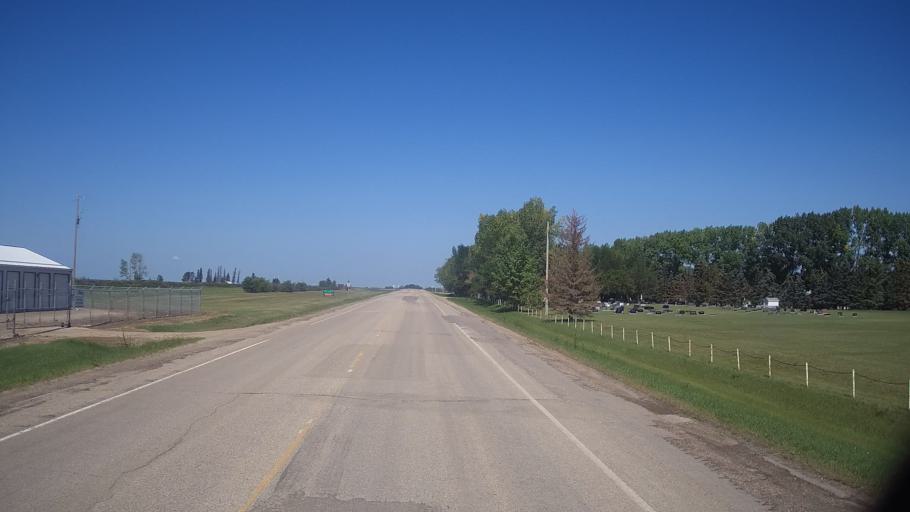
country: CA
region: Saskatchewan
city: Saskatoon
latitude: 51.8950
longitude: -106.0618
